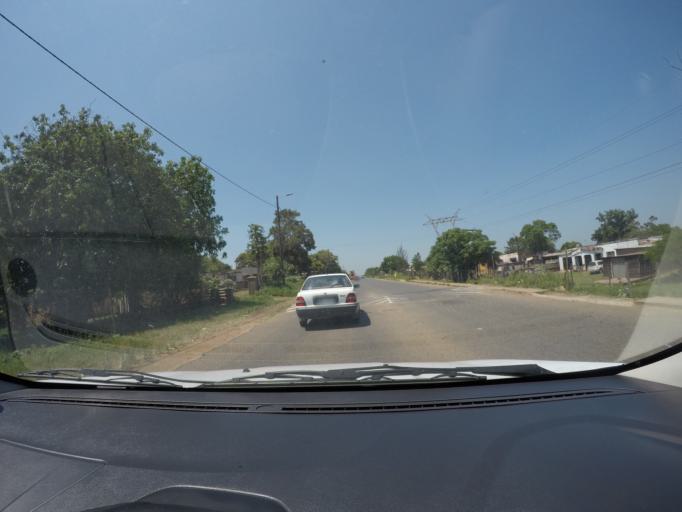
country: ZA
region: KwaZulu-Natal
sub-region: uThungulu District Municipality
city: eSikhawini
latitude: -28.8262
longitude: 31.9445
